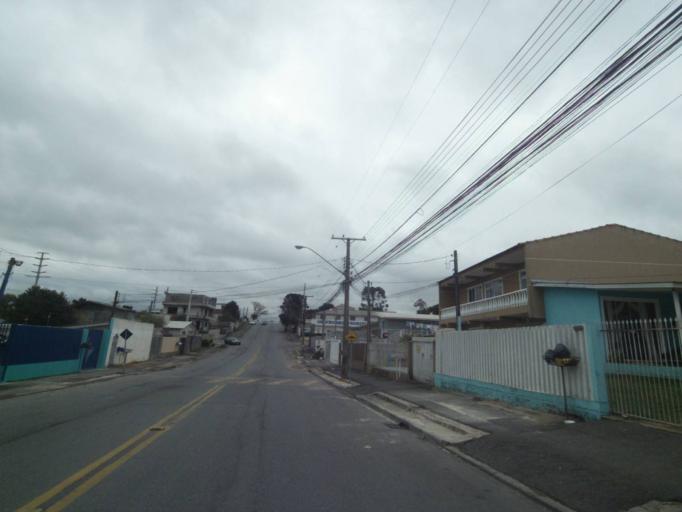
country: BR
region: Parana
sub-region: Sao Jose Dos Pinhais
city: Sao Jose dos Pinhais
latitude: -25.5211
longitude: -49.3035
